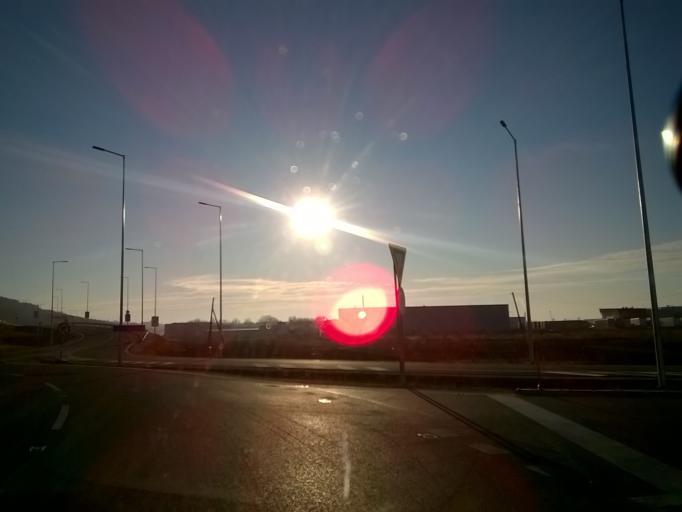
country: SK
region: Nitriansky
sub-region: Okres Nitra
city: Nitra
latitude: 48.3409
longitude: 18.0593
